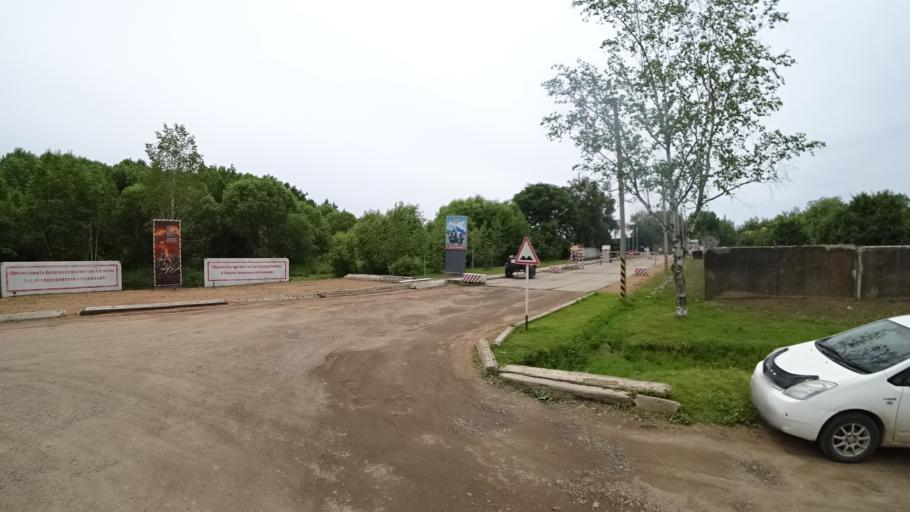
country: RU
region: Primorskiy
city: Novosysoyevka
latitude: 44.2009
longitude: 133.3174
